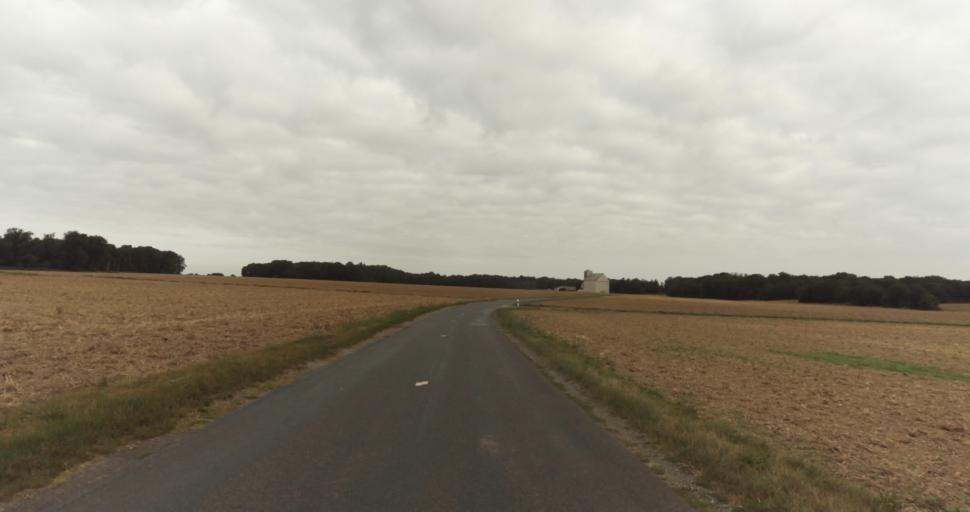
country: FR
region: Haute-Normandie
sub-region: Departement de l'Eure
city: Saint-Germain-sur-Avre
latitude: 48.7945
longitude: 1.2807
